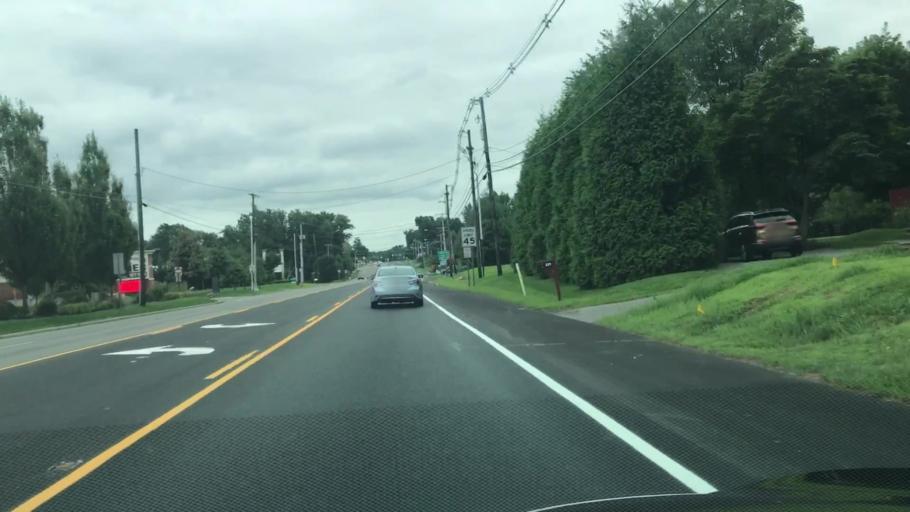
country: US
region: New Jersey
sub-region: Hunterdon County
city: Flemington
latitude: 40.5411
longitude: -74.8574
